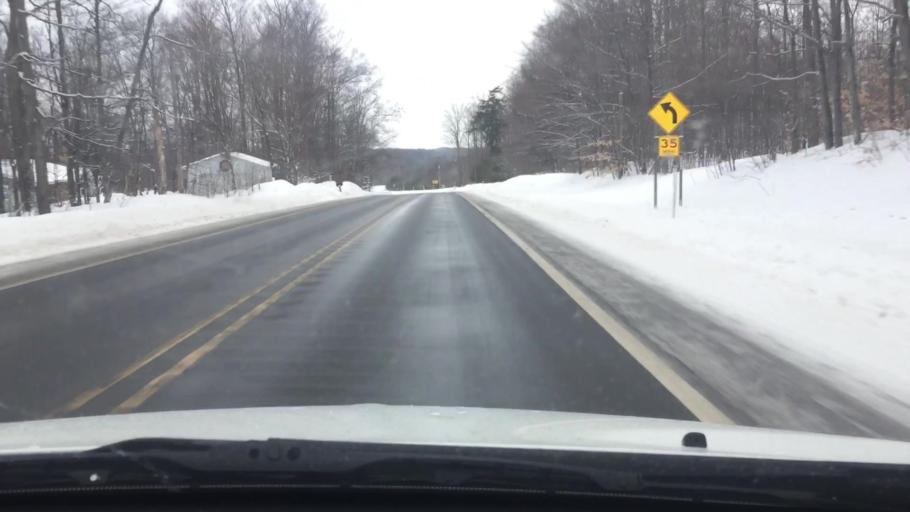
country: US
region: Michigan
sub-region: Charlevoix County
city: East Jordan
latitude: 45.1018
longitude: -85.0295
